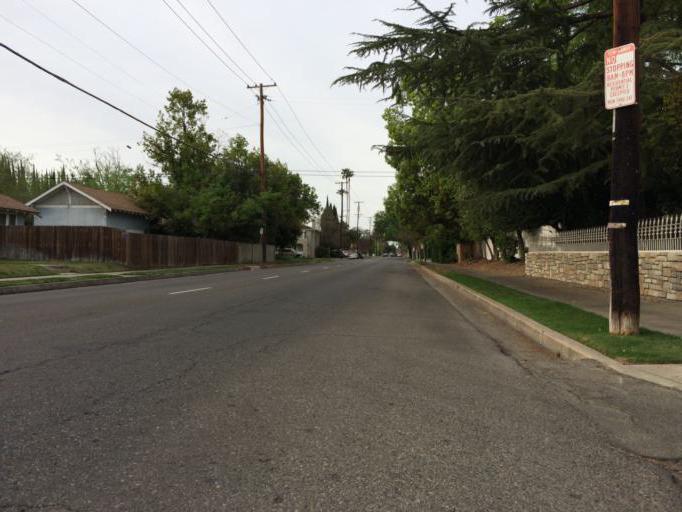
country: US
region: California
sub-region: Fresno County
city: Fresno
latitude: 36.7695
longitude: -119.7995
